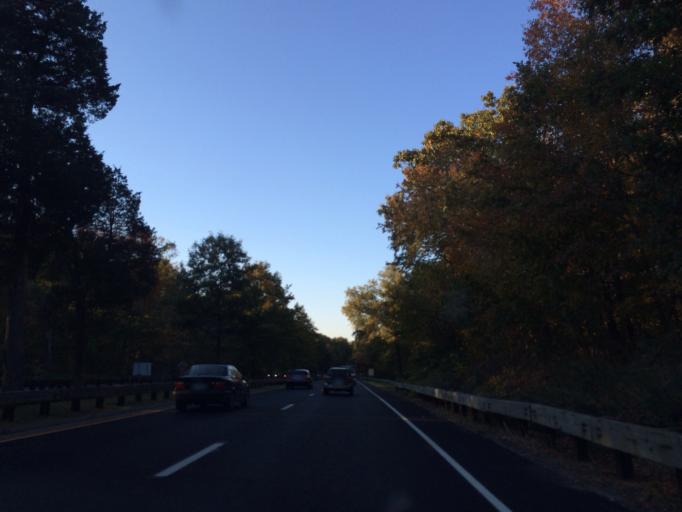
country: US
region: Connecticut
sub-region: Fairfield County
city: Glenville
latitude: 41.0472
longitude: -73.6703
